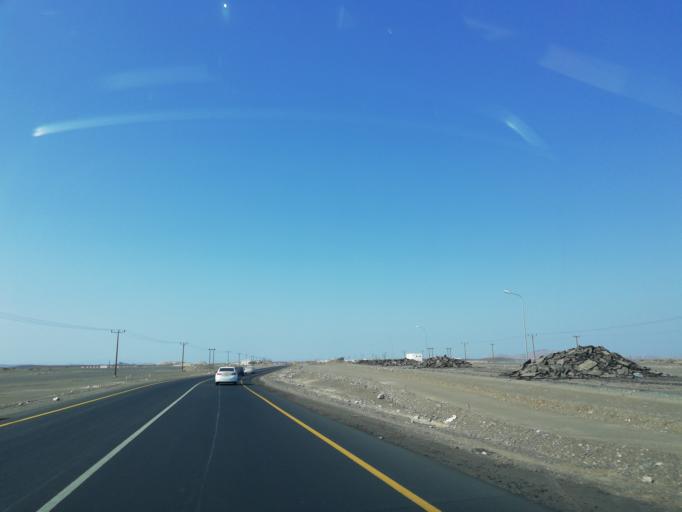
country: OM
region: Ash Sharqiyah
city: Ibra'
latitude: 22.7099
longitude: 58.1437
